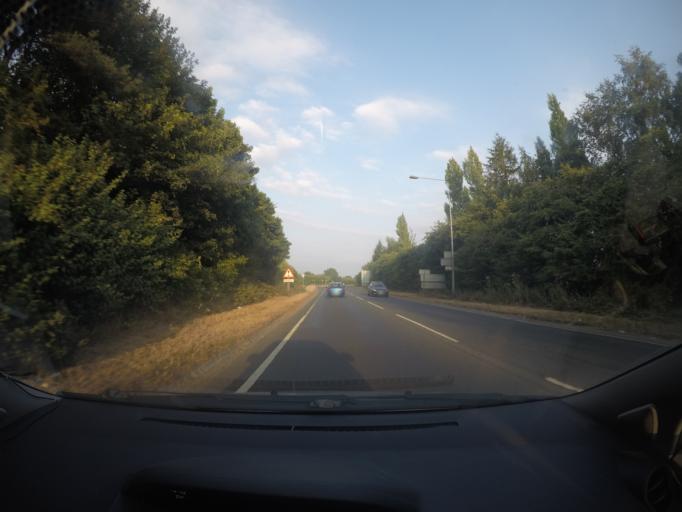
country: GB
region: England
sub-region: City of York
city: Huntington
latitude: 54.0045
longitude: -1.0546
